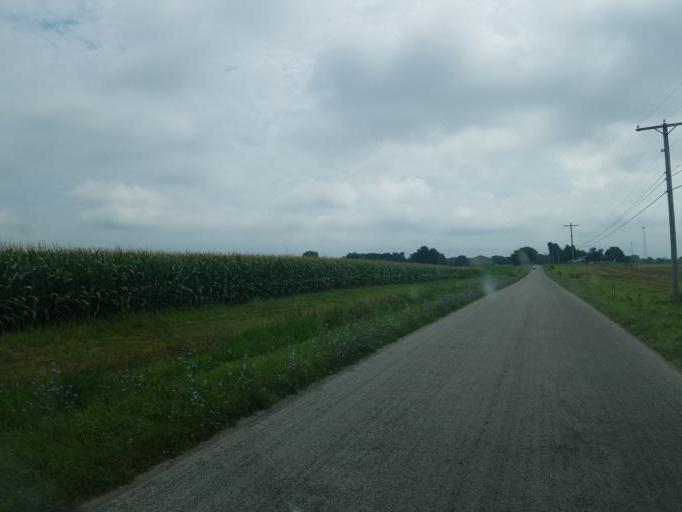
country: US
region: Ohio
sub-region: Morrow County
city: Cardington
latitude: 40.4152
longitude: -82.8334
